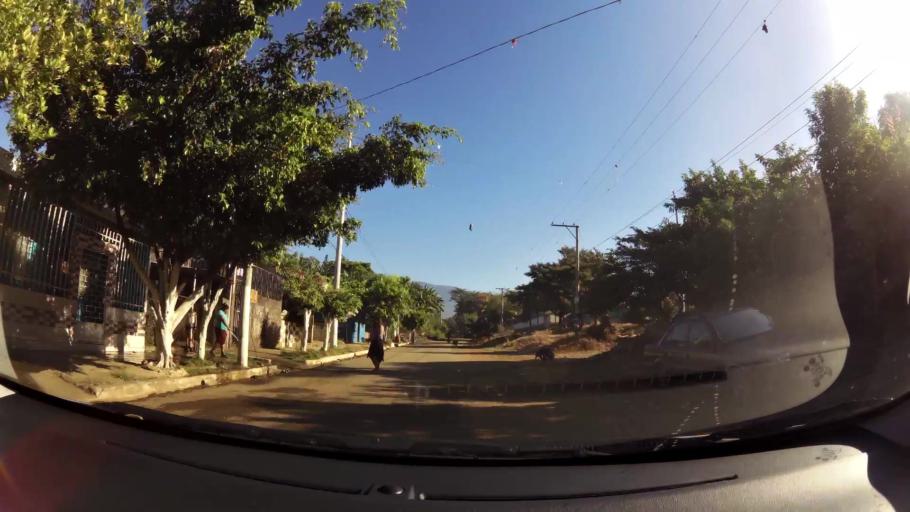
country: SV
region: Sonsonate
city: Sonzacate
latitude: 13.7421
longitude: -89.7118
